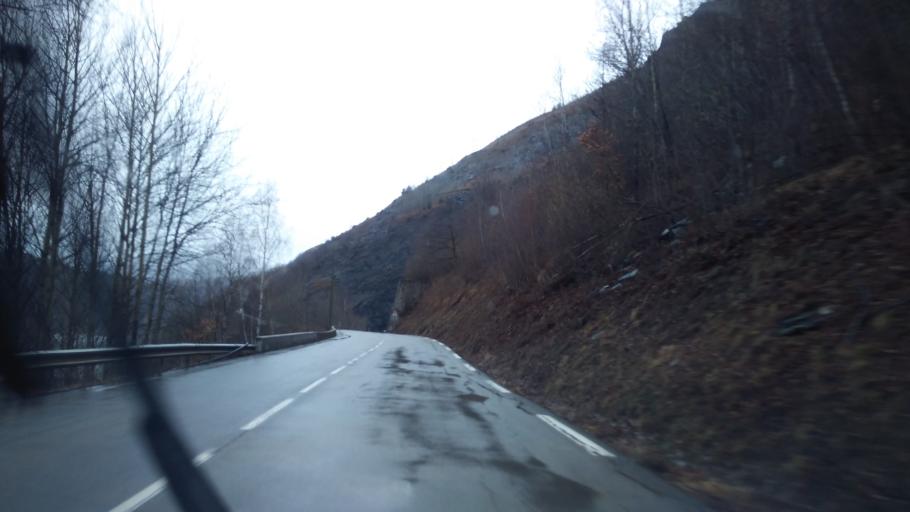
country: FR
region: Rhone-Alpes
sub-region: Departement de l'Isere
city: Mont-de-Lans
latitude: 45.0428
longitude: 6.1668
